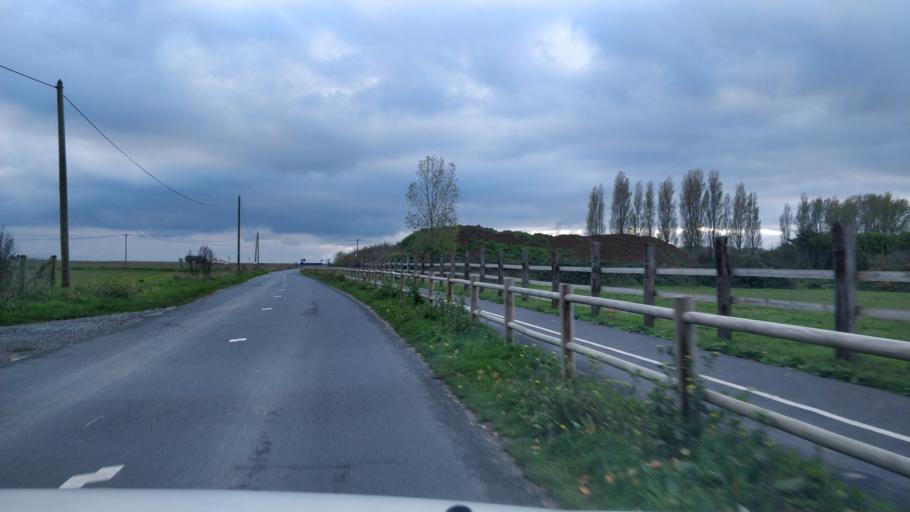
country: FR
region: Lower Normandy
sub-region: Departement du Calvados
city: Ouistreham
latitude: 49.2705
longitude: -0.2668
